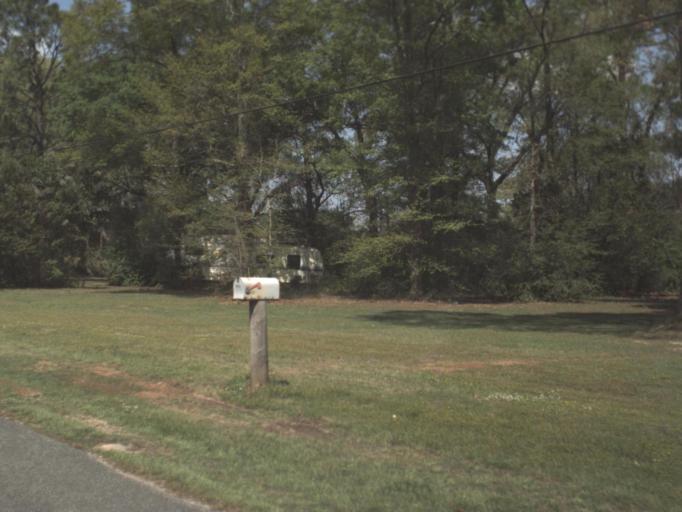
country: US
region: Florida
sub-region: Escambia County
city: Century
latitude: 30.9522
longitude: -87.1151
